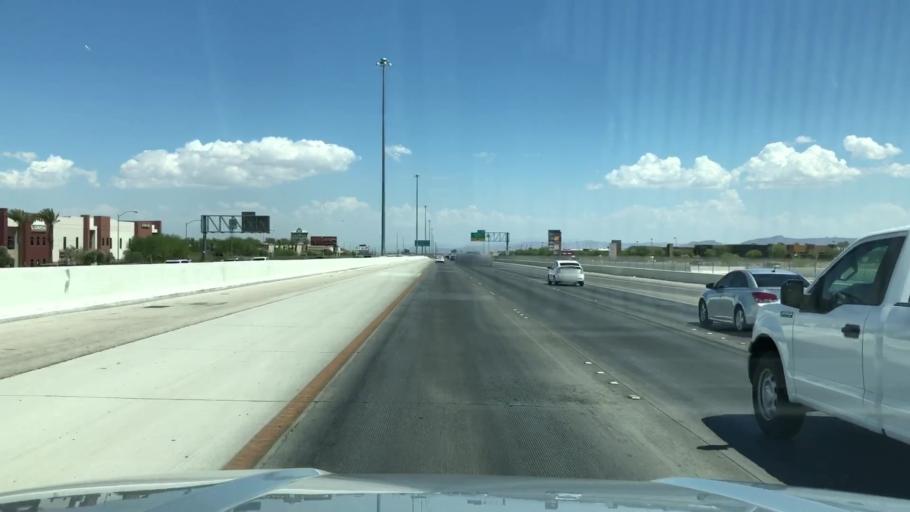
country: US
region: Nevada
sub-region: Clark County
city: Spring Valley
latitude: 36.0662
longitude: -115.2561
